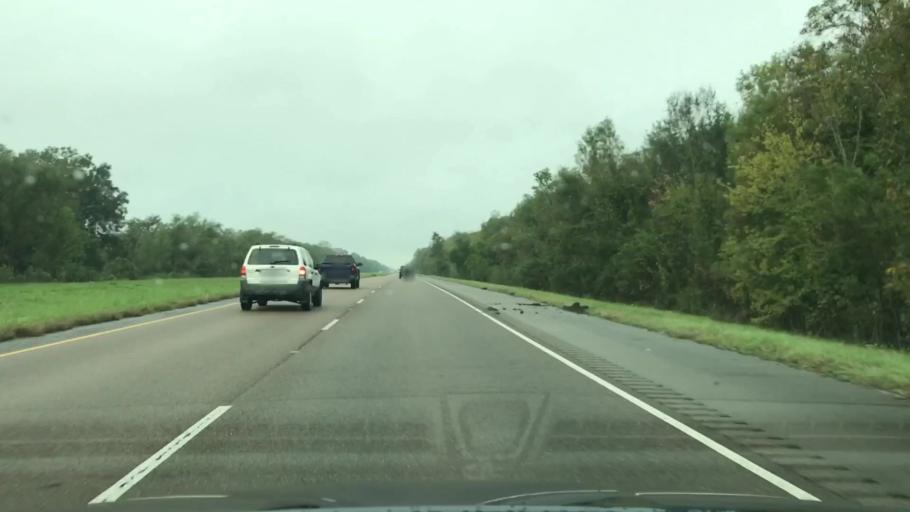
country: US
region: Louisiana
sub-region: Terrebonne Parish
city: Gray
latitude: 29.6859
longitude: -90.7171
